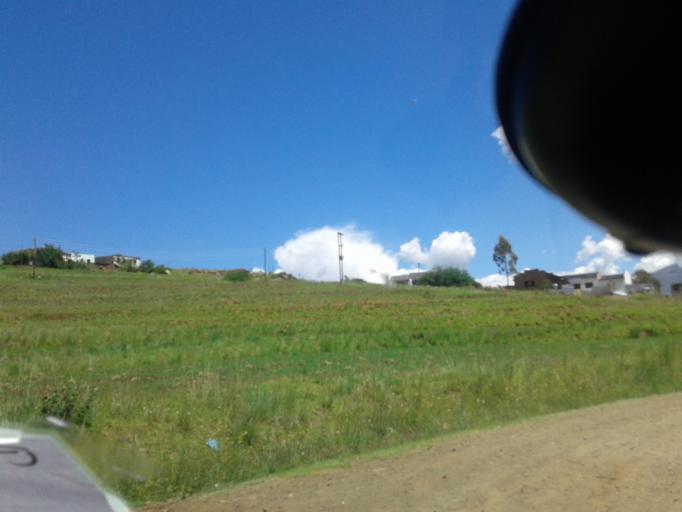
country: LS
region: Qacha's Nek
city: Qacha's Nek
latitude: -30.0925
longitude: 28.6432
